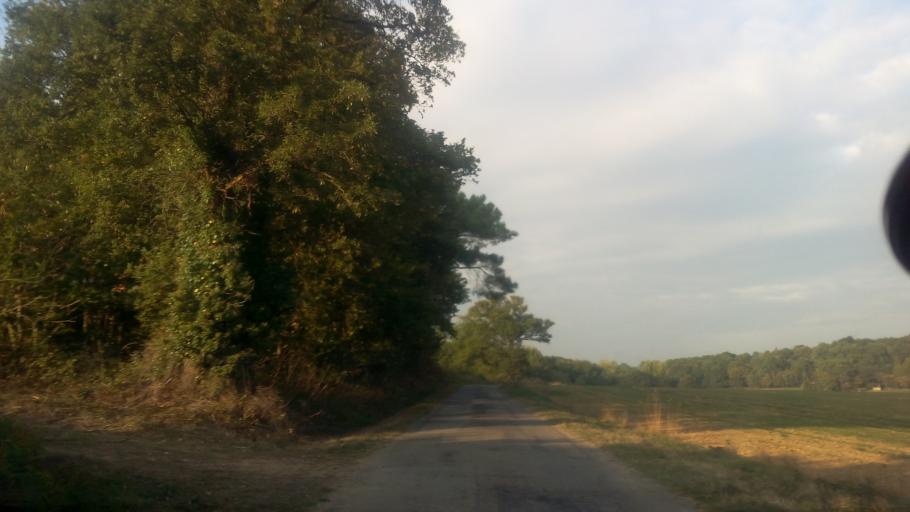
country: FR
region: Brittany
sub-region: Departement du Morbihan
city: Saint-Jean-la-Poterie
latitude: 47.6277
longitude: -2.1266
